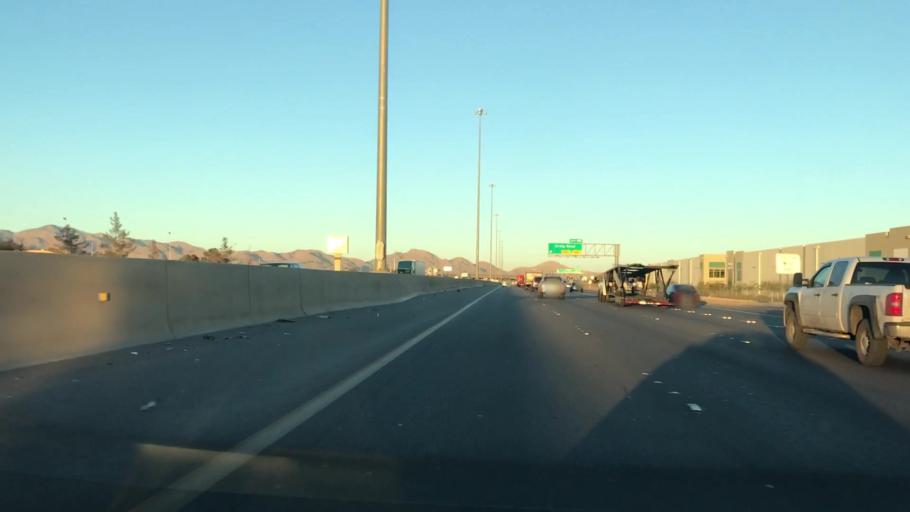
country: US
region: Nevada
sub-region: Clark County
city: North Las Vegas
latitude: 36.2355
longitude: -115.1083
